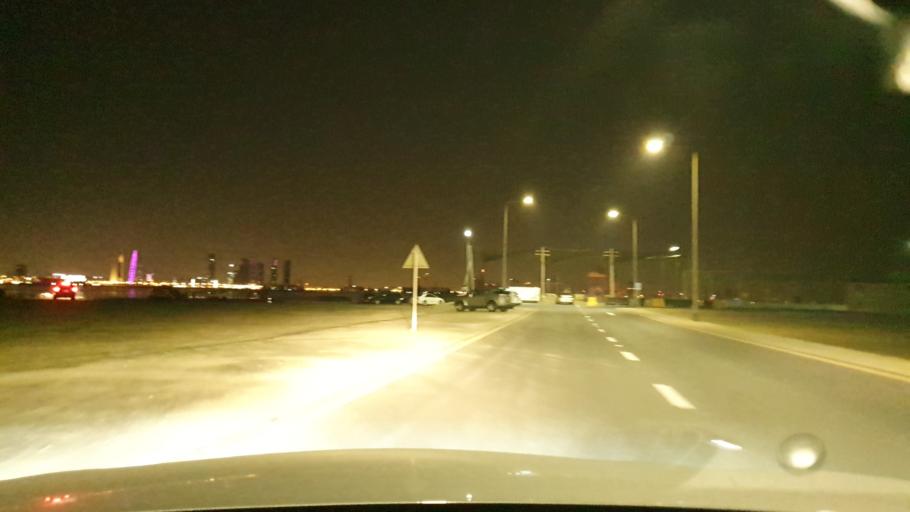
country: BH
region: Muharraq
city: Al Muharraq
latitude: 26.2844
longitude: 50.5776
